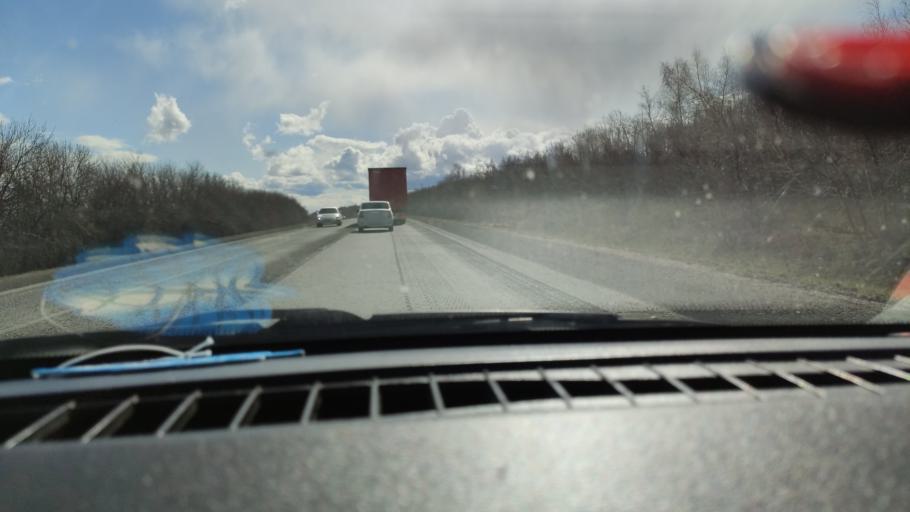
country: RU
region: Saratov
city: Dukhovnitskoye
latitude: 52.6482
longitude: 48.1976
